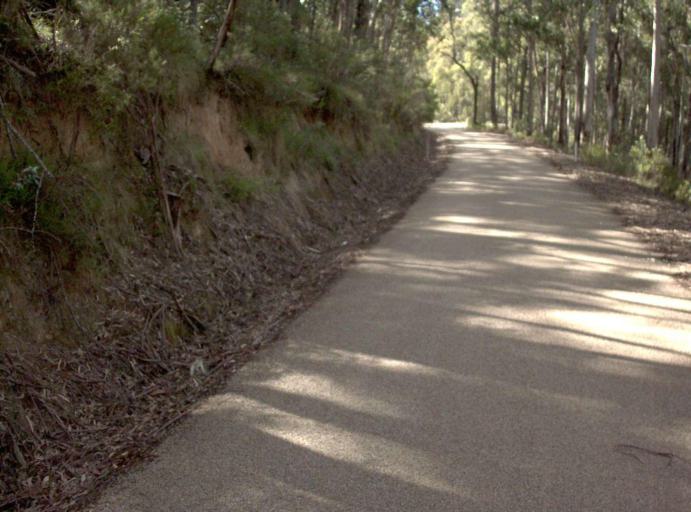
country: AU
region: Victoria
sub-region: East Gippsland
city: Lakes Entrance
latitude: -37.4019
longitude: 148.1265
